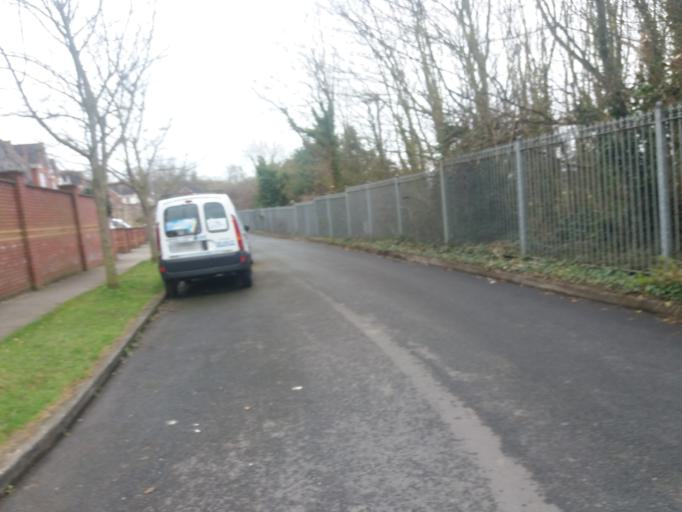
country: IE
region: Leinster
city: Portmarnock
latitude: 53.4366
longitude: -6.1420
